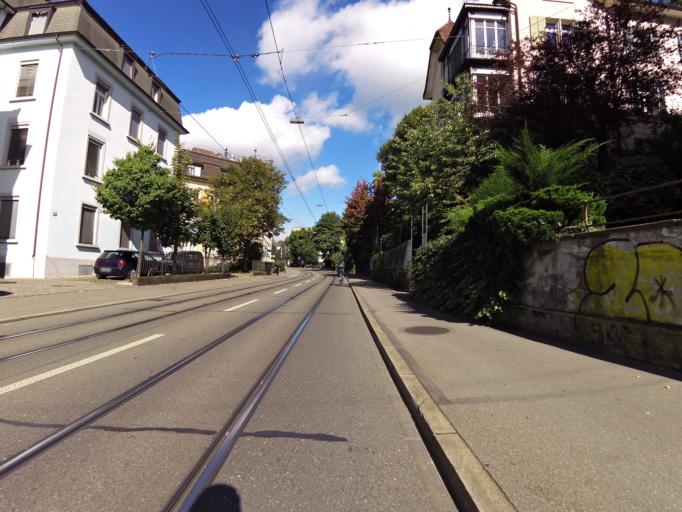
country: CH
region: Zurich
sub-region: Bezirk Zuerich
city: Zuerich (Kreis 6)
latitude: 47.3835
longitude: 8.5433
